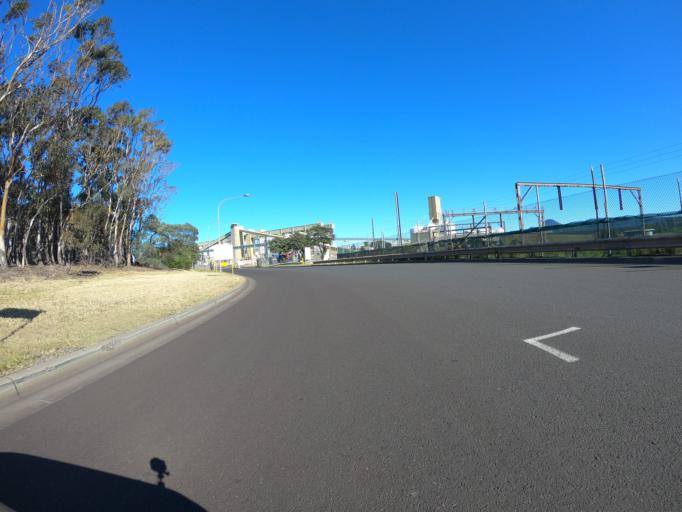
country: AU
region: New South Wales
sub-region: Wollongong
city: Coniston
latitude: -34.4480
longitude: 150.8967
